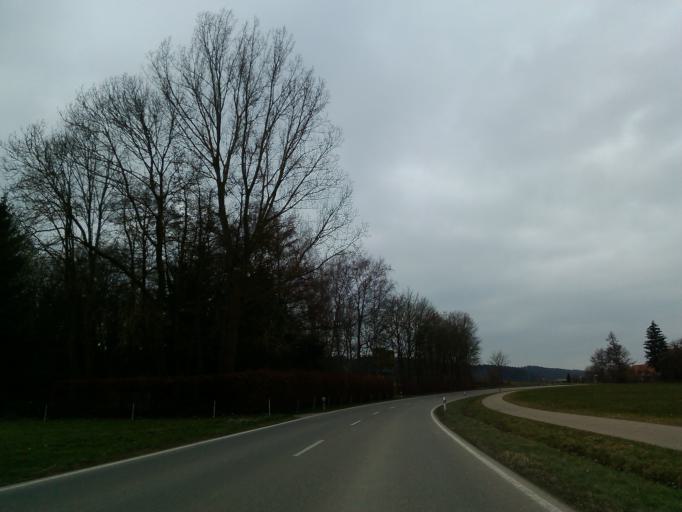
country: DE
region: Bavaria
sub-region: Swabia
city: Ustersbach
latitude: 48.3106
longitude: 10.6284
